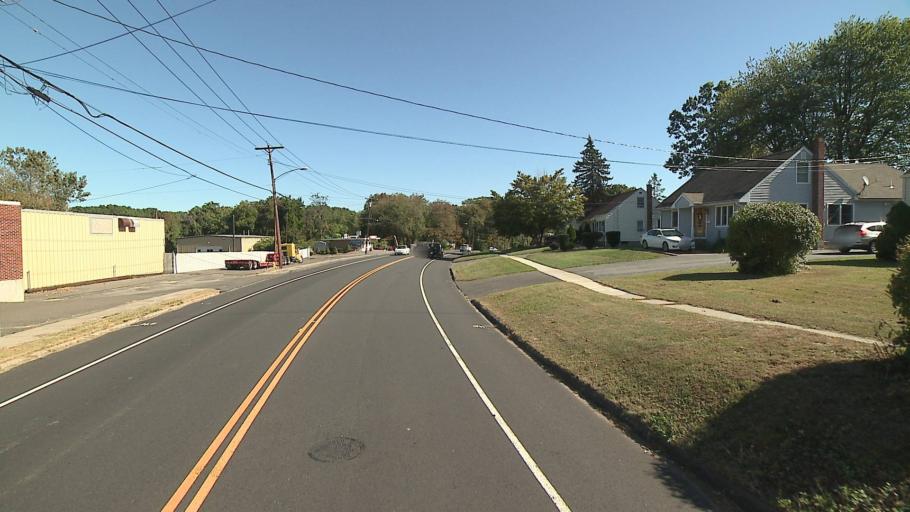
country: US
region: Connecticut
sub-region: New Haven County
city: Milford
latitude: 41.2263
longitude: -73.0272
